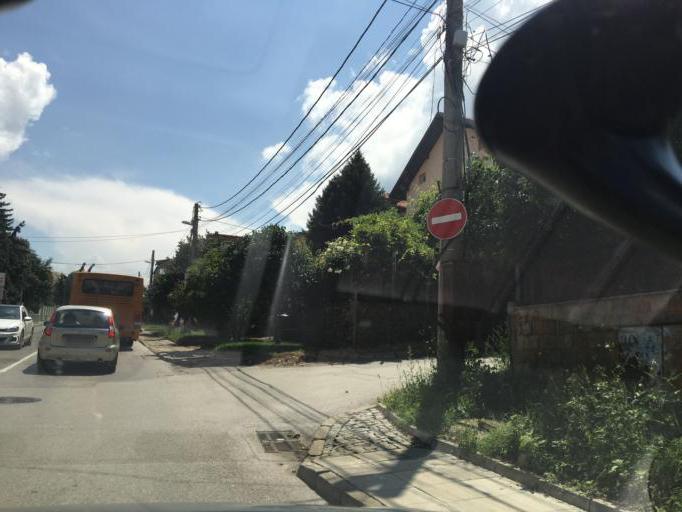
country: BG
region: Sofia-Capital
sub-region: Stolichna Obshtina
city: Sofia
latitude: 42.6190
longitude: 23.3357
